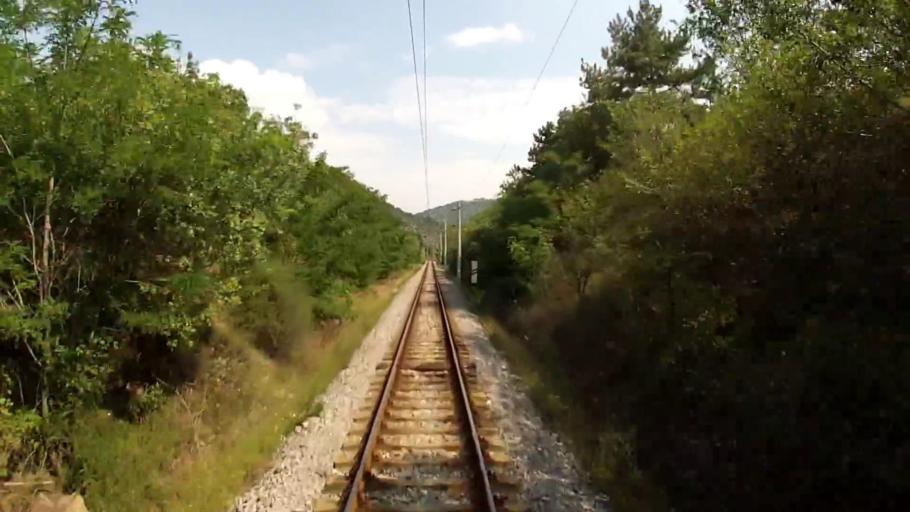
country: BG
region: Blagoevgrad
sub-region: Obshtina Kresna
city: Kresna
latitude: 41.7192
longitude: 23.1645
